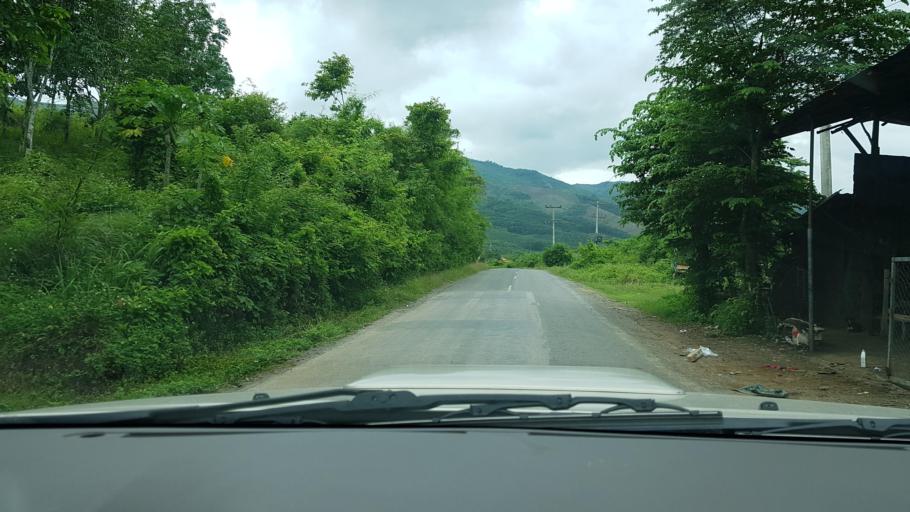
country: LA
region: Loungnamtha
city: Muang Nale
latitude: 20.2495
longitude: 101.5767
